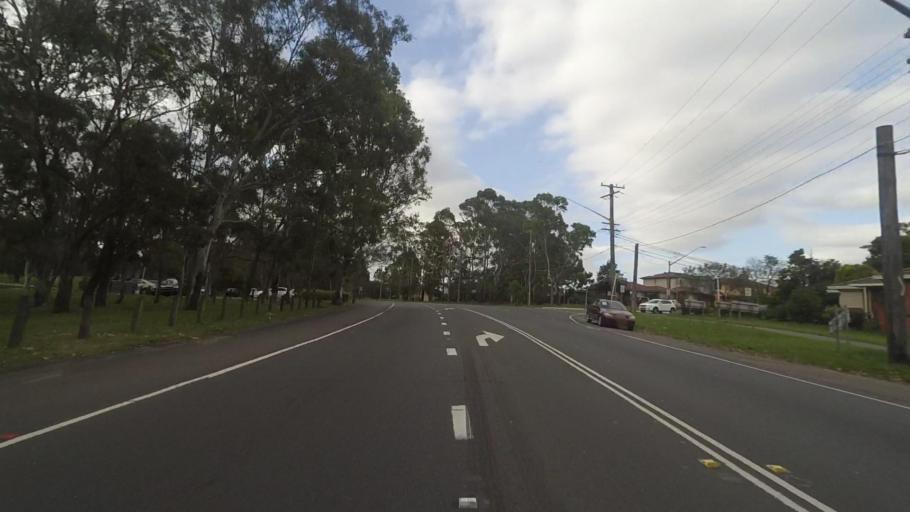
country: AU
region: New South Wales
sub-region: Fairfield
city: Carramar
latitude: -33.9074
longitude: 150.9820
